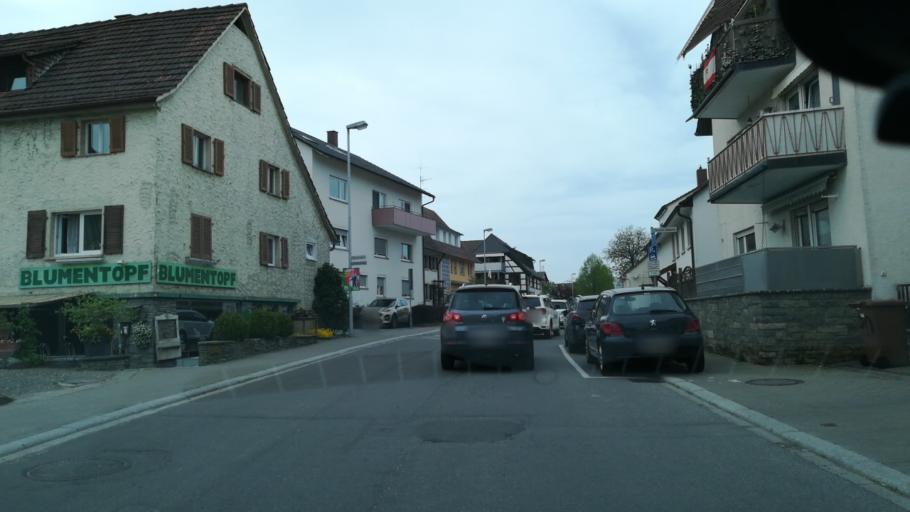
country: DE
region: Baden-Wuerttemberg
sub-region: Freiburg Region
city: Konstanz
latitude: 47.7144
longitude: 9.1726
